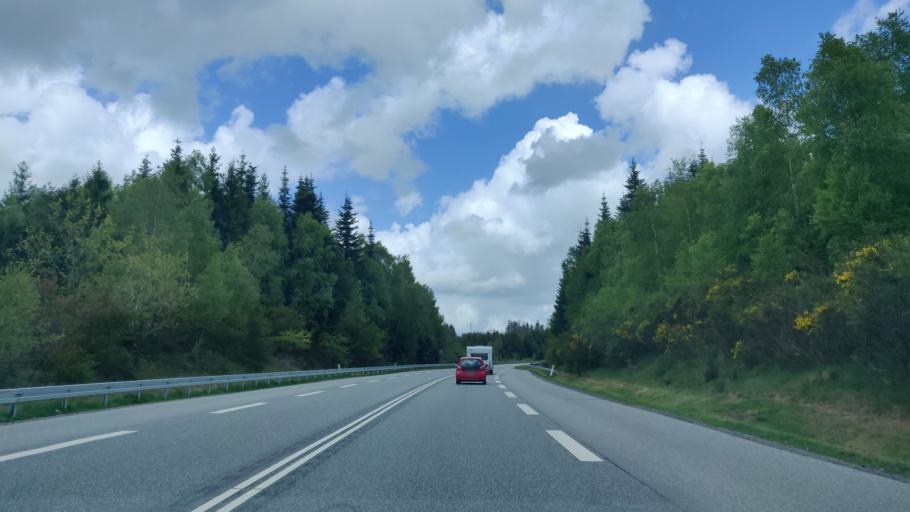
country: DK
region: Central Jutland
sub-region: Hedensted Kommune
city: Torring
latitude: 55.9541
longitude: 9.3974
